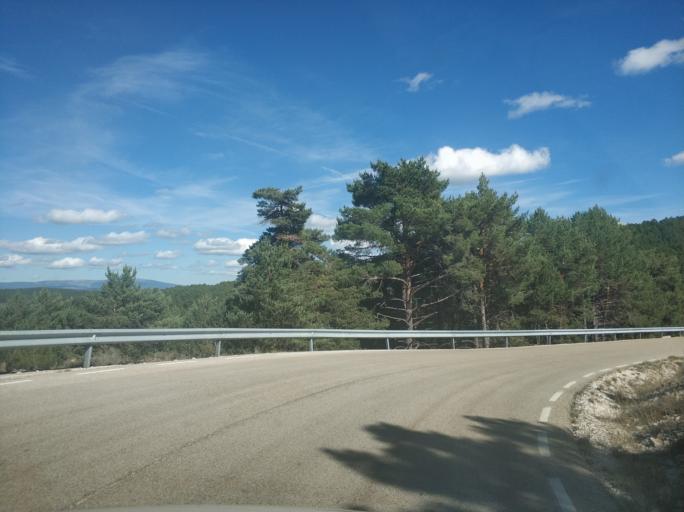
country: ES
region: Castille and Leon
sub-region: Provincia de Soria
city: Espejon
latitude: 41.8410
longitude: -3.2397
